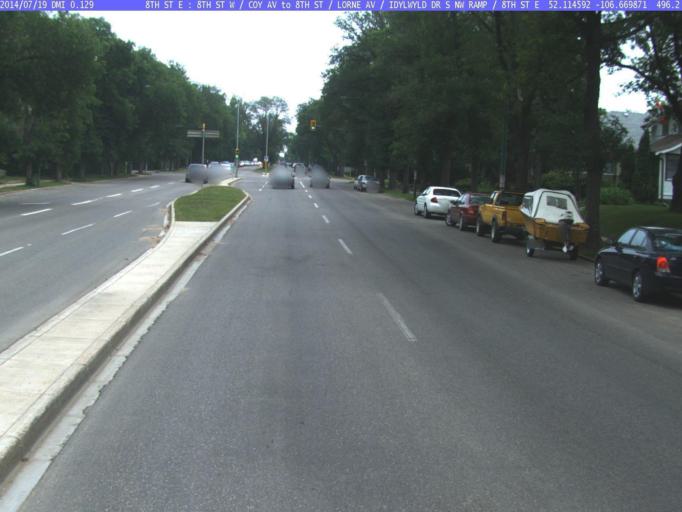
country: CA
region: Saskatchewan
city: Saskatoon
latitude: 52.1146
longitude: -106.6699
